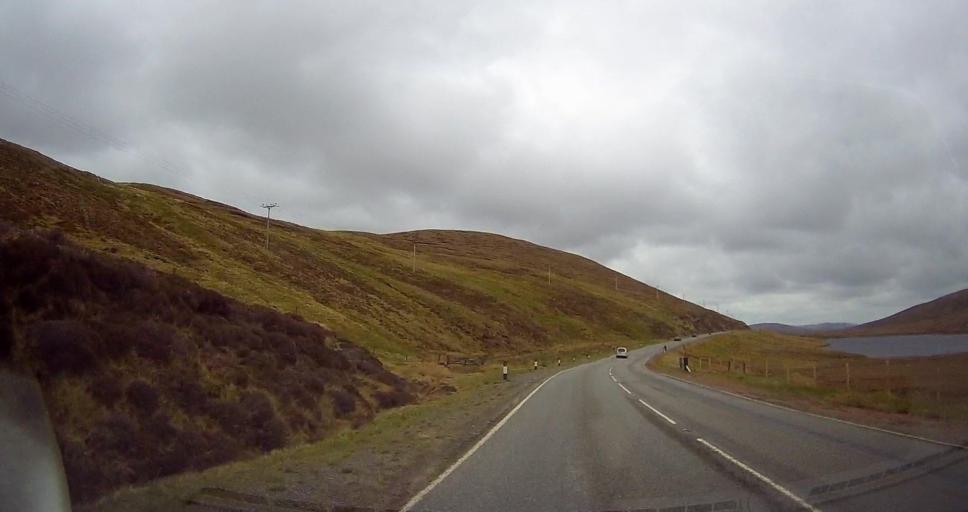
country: GB
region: Scotland
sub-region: Shetland Islands
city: Lerwick
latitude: 60.3191
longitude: -1.2479
